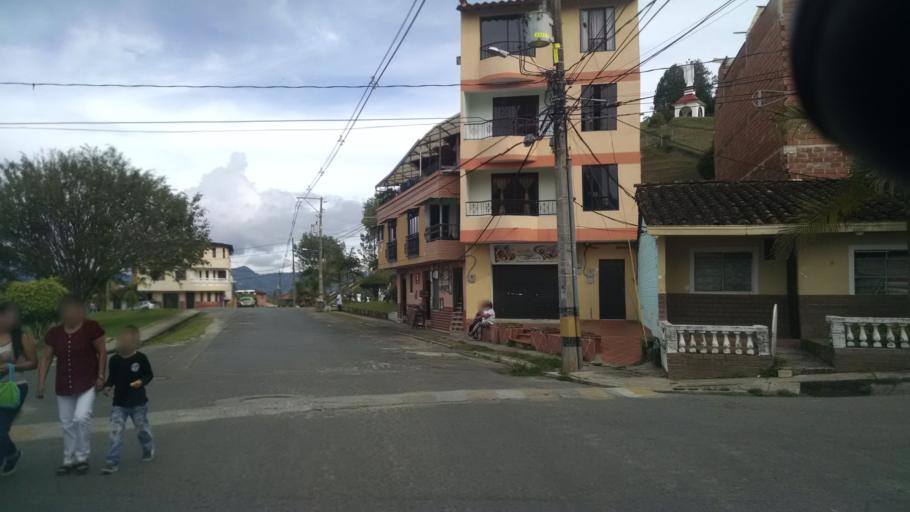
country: CO
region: Antioquia
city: Santuario
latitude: 6.2153
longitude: -75.2422
